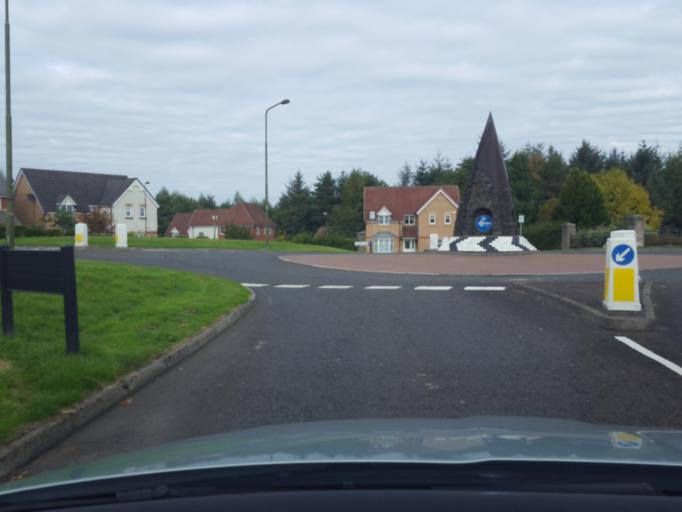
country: GB
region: Scotland
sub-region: West Lothian
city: Livingston
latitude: 55.8745
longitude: -3.5294
